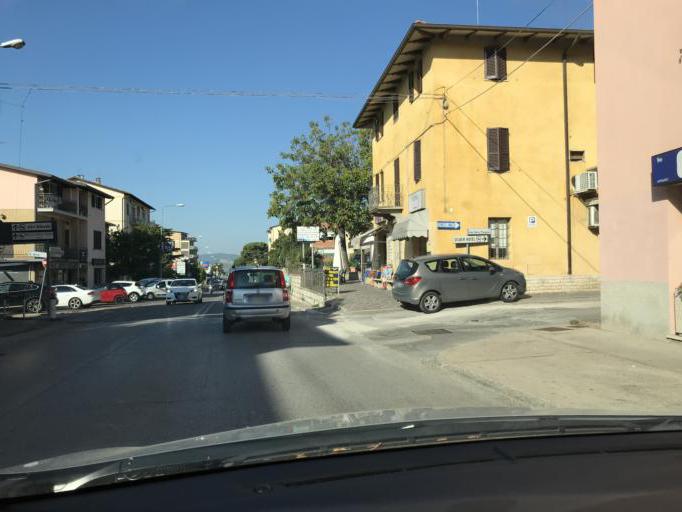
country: IT
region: Umbria
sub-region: Provincia di Perugia
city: Lacugnano
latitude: 43.1043
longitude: 12.3212
